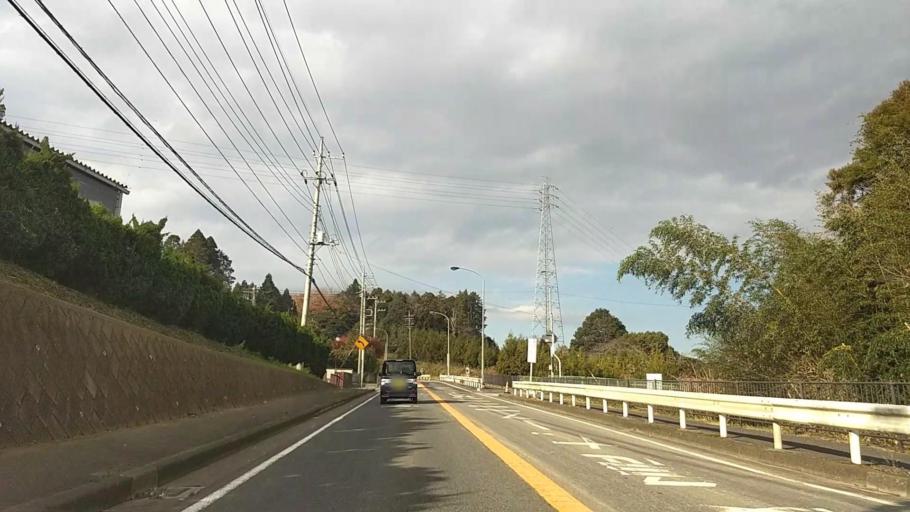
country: JP
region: Chiba
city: Oami
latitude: 35.5744
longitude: 140.3050
